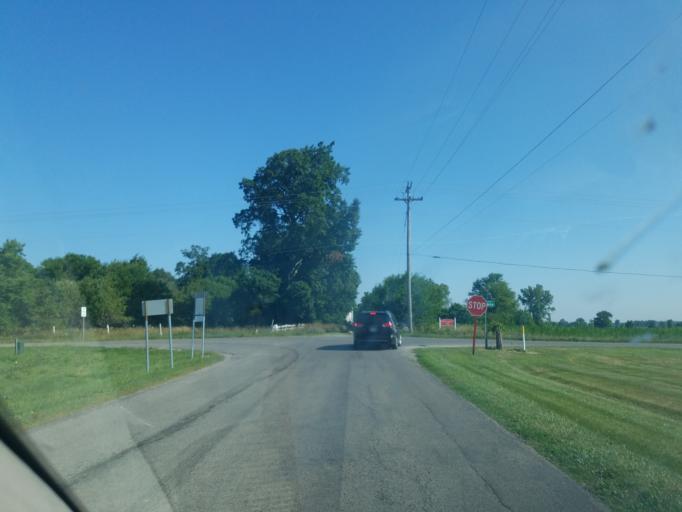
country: US
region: Ohio
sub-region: Union County
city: Richwood
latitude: 40.4377
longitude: -83.3045
